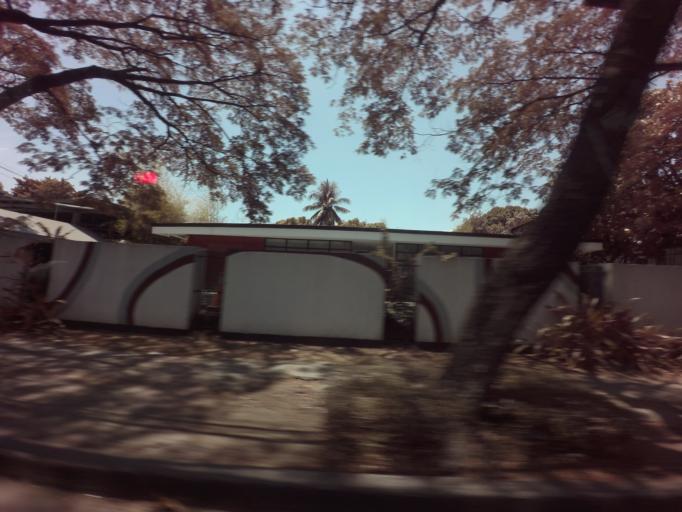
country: PH
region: Metro Manila
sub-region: Makati City
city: Makati City
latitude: 14.5593
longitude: 121.0300
